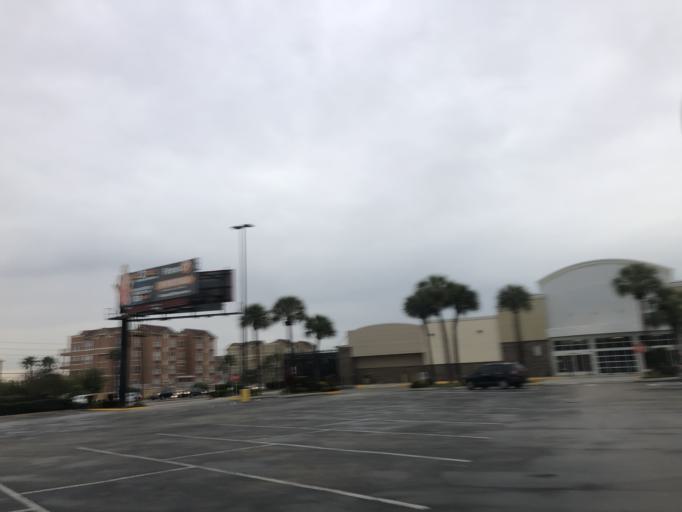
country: US
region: Florida
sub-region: Orange County
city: Doctor Phillips
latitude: 28.4535
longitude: -81.4770
